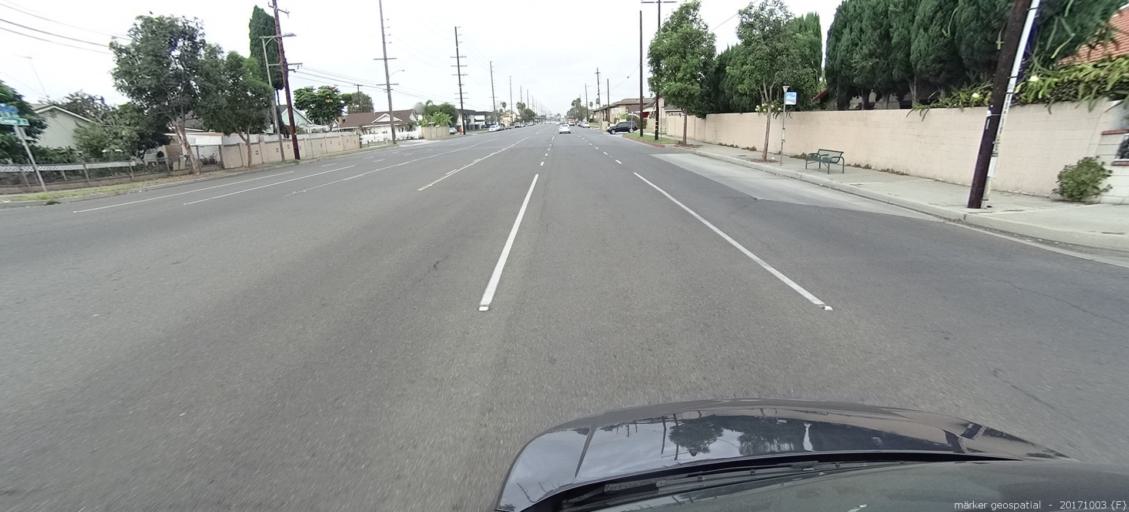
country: US
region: California
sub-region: Orange County
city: Garden Grove
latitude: 33.7451
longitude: -117.9414
